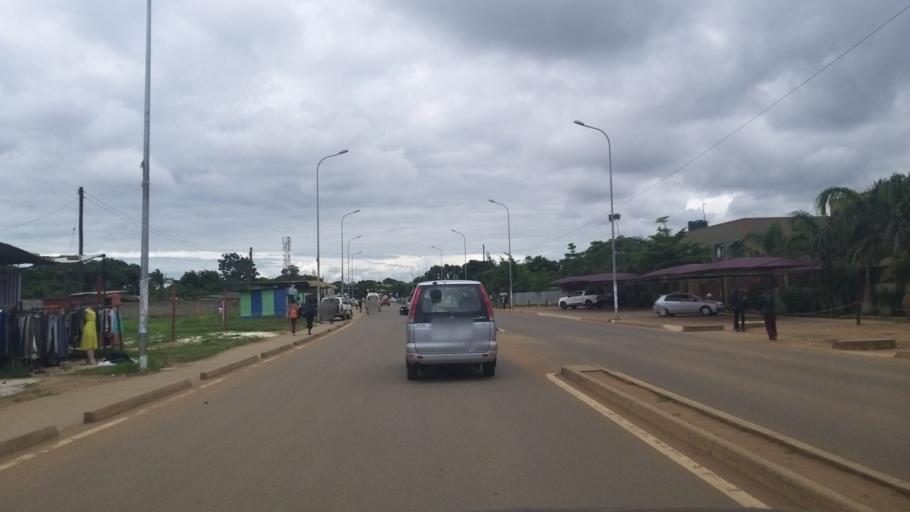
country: ZM
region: Lusaka
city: Lusaka
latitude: -15.4392
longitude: 28.3111
